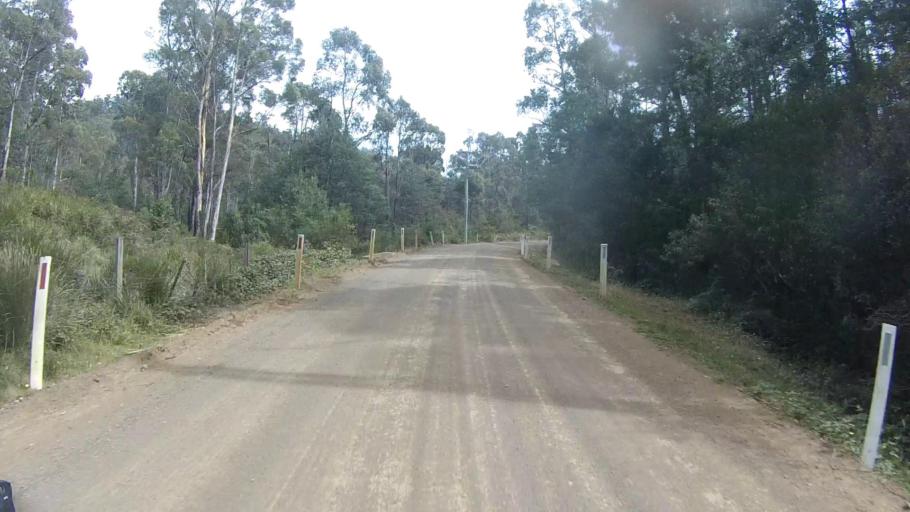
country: AU
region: Tasmania
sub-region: Sorell
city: Sorell
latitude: -42.7680
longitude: 147.8058
